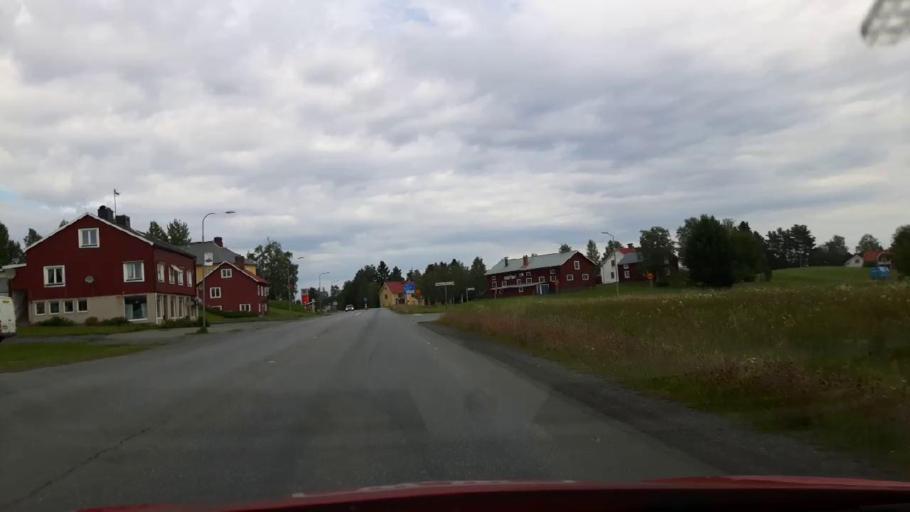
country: SE
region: Jaemtland
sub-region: Stroemsunds Kommun
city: Stroemsund
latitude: 63.5900
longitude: 15.3546
